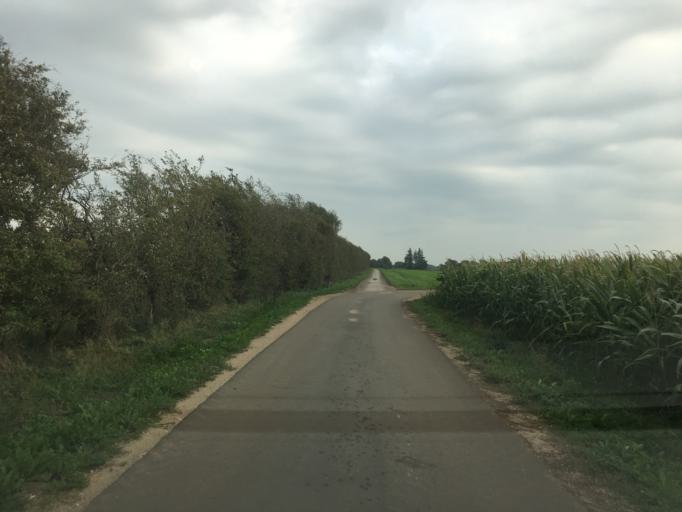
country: DK
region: South Denmark
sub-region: Tonder Kommune
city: Logumkloster
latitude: 55.0028
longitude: 9.0563
